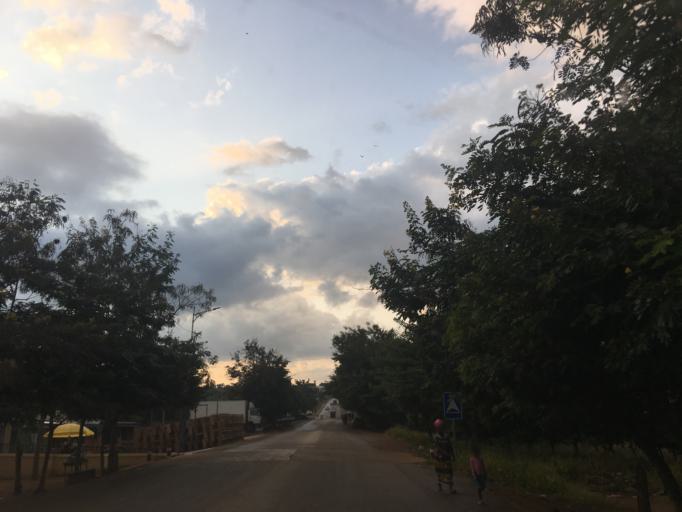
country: GH
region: Western
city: Bibiani
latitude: 6.7781
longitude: -2.5140
